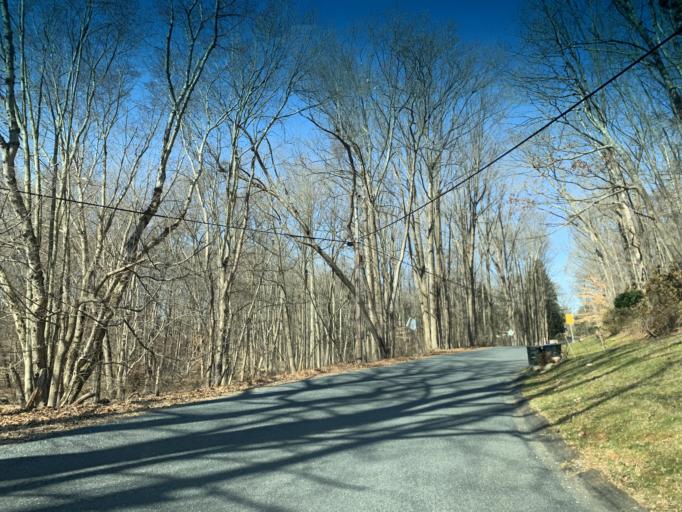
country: US
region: Maryland
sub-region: Harford County
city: Fallston
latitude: 39.5136
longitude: -76.4404
